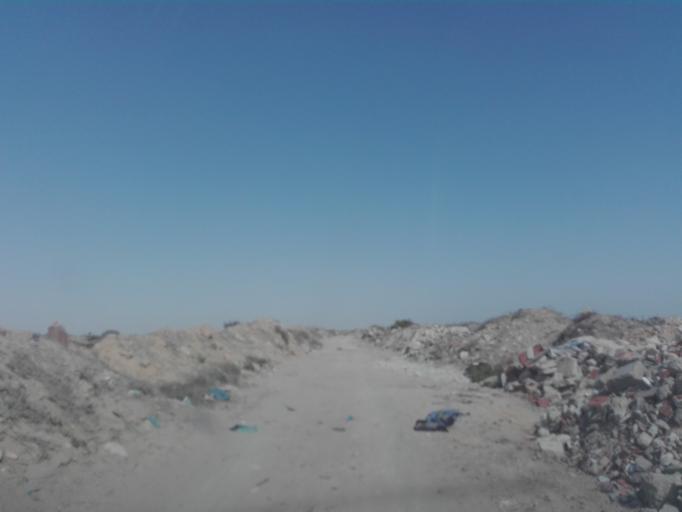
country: TN
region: Qabis
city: Gabes
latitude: 33.9607
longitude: 10.0668
